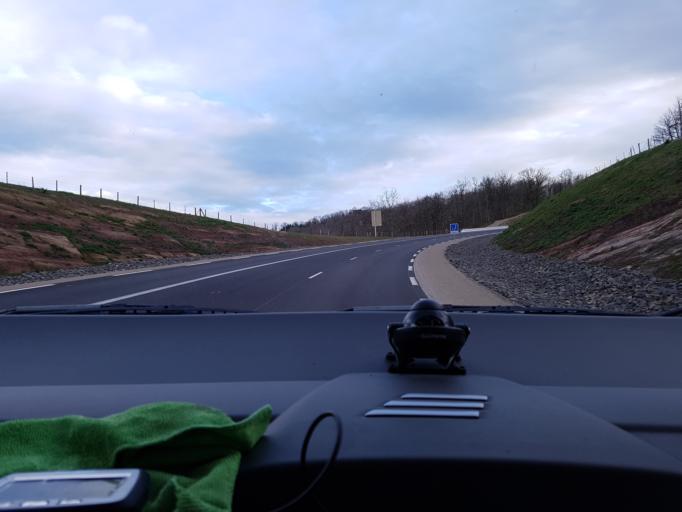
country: FR
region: Midi-Pyrenees
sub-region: Departement de l'Aveyron
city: Espalion
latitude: 44.5222
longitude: 2.7340
